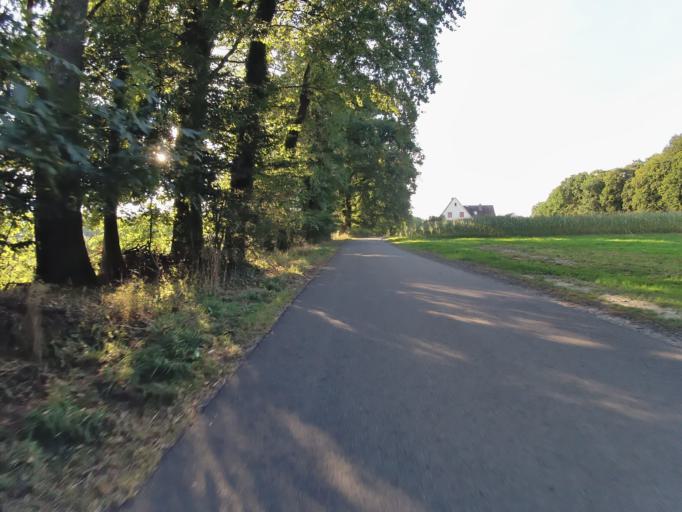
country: DE
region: North Rhine-Westphalia
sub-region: Regierungsbezirk Munster
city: Westerkappeln
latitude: 52.3605
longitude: 7.8517
